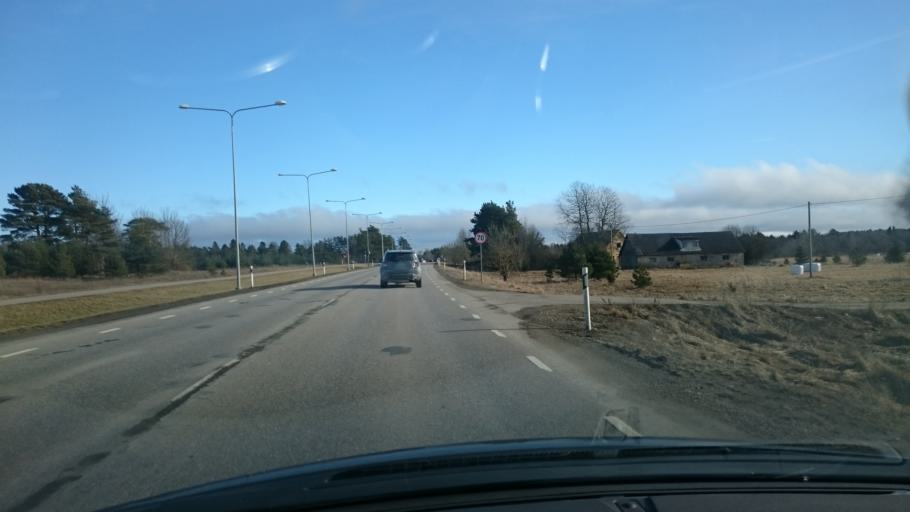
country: EE
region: Harju
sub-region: Harku vald
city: Tabasalu
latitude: 59.4413
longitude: 24.4935
